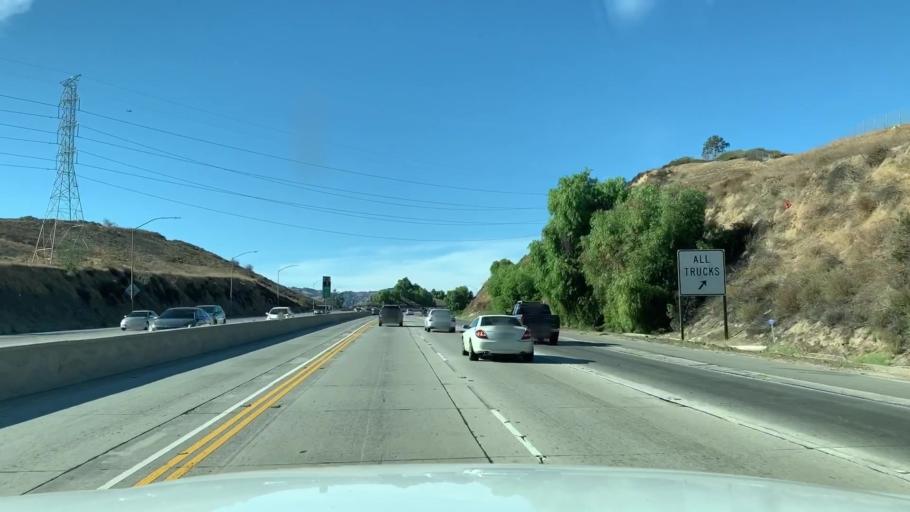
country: US
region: California
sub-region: Los Angeles County
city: San Fernando
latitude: 34.2864
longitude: -118.4618
